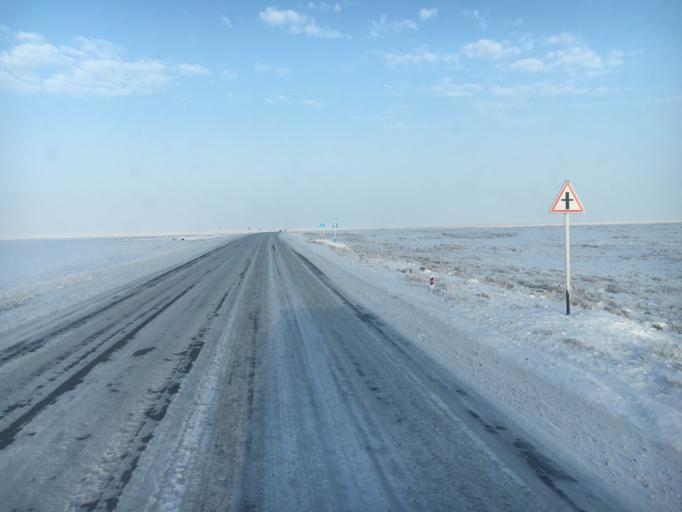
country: KZ
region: Aqtoebe
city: Yrghyz
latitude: 47.9551
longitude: 61.2629
